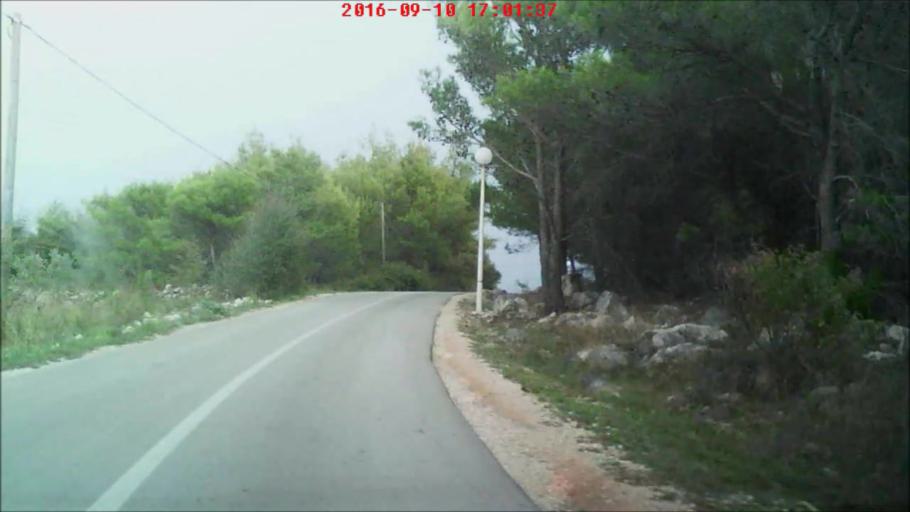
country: HR
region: Zadarska
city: Vir
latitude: 44.3067
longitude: 15.0590
